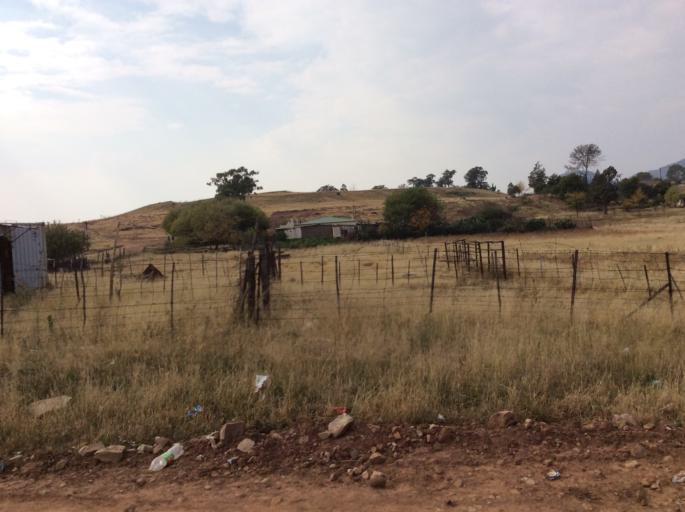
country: LS
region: Mafeteng
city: Mafeteng
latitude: -29.9880
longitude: 27.0016
